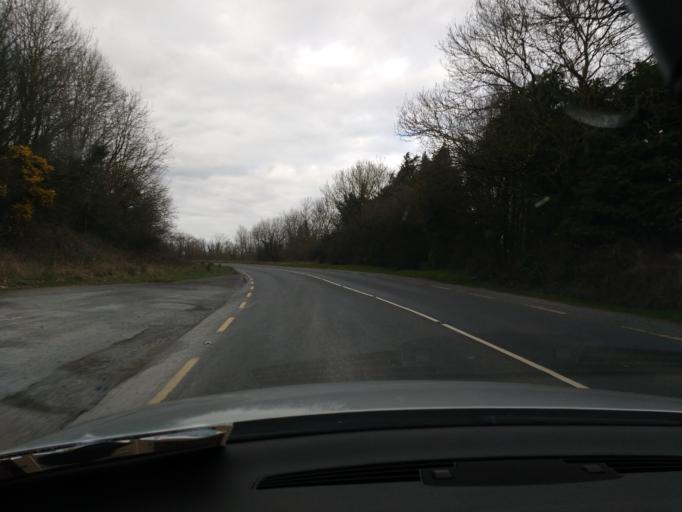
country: IE
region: Leinster
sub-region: Kilkenny
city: Kilkenny
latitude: 52.6902
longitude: -7.2766
